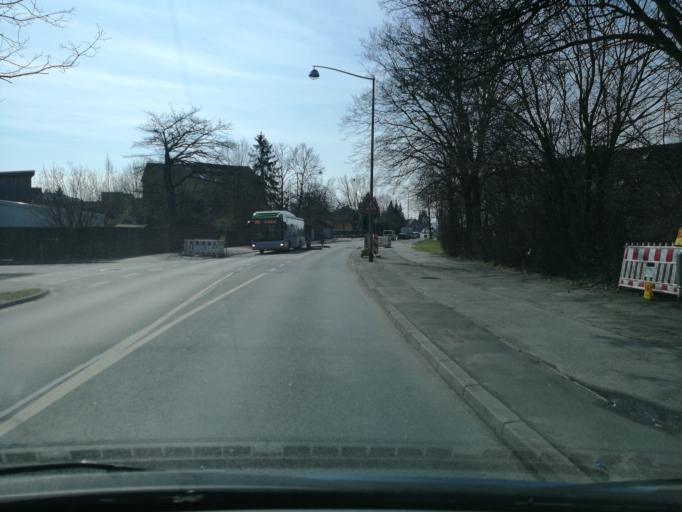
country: DE
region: Lower Saxony
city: Ronnenberg
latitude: 52.3678
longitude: 9.6708
